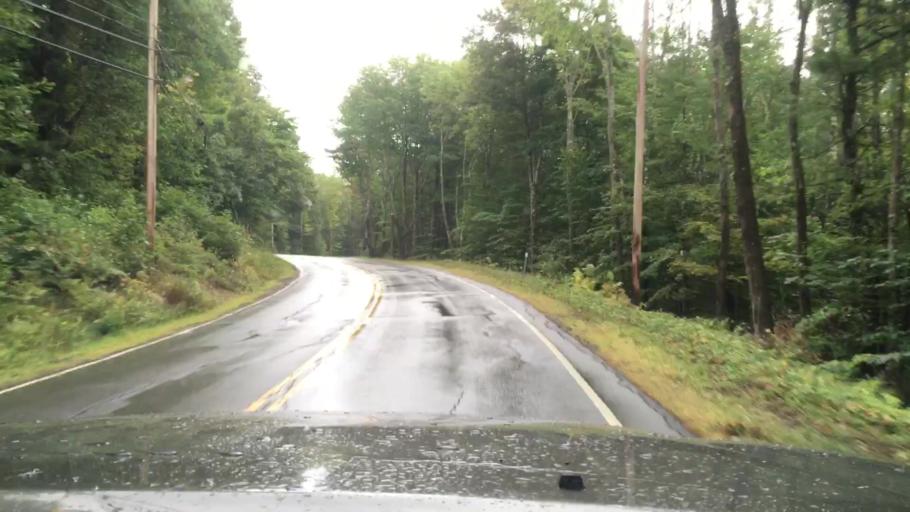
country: US
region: New Hampshire
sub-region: Belknap County
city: Meredith
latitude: 43.6472
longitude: -71.5399
